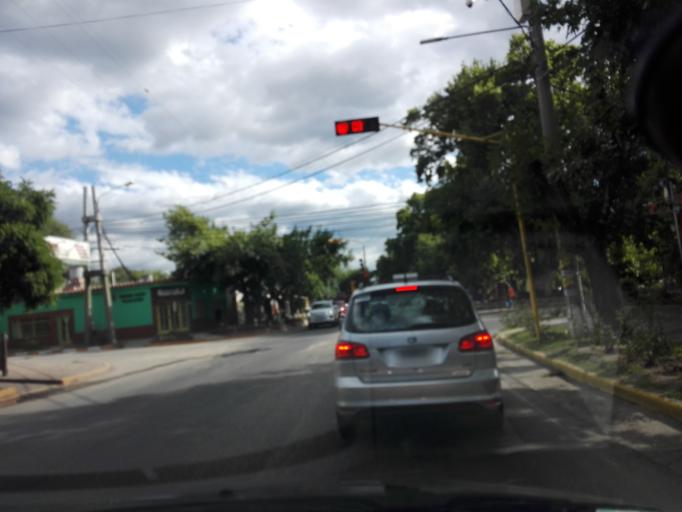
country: AR
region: Cordoba
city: Villa Las Rosas
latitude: -31.9465
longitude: -65.0511
